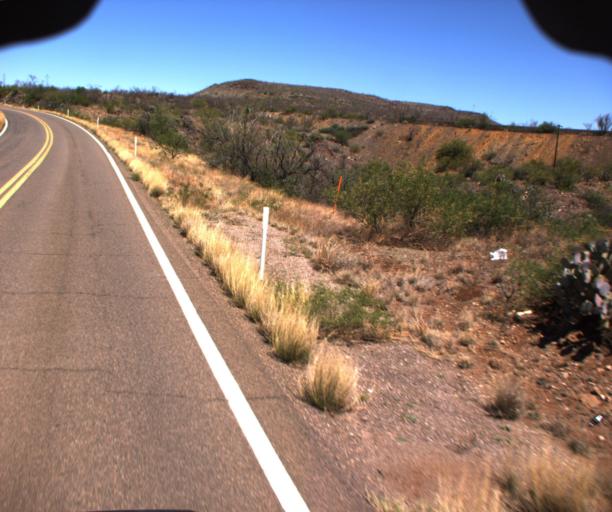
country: US
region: Arizona
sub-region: Cochise County
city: Douglas
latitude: 31.4632
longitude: -109.3813
